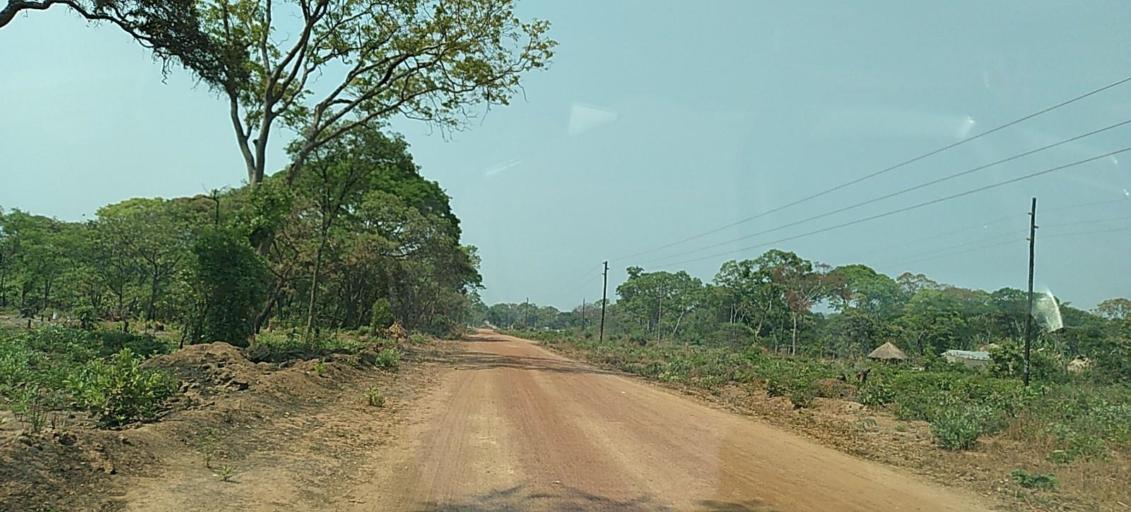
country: ZM
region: Copperbelt
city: Kalulushi
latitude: -13.1040
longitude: 27.4033
